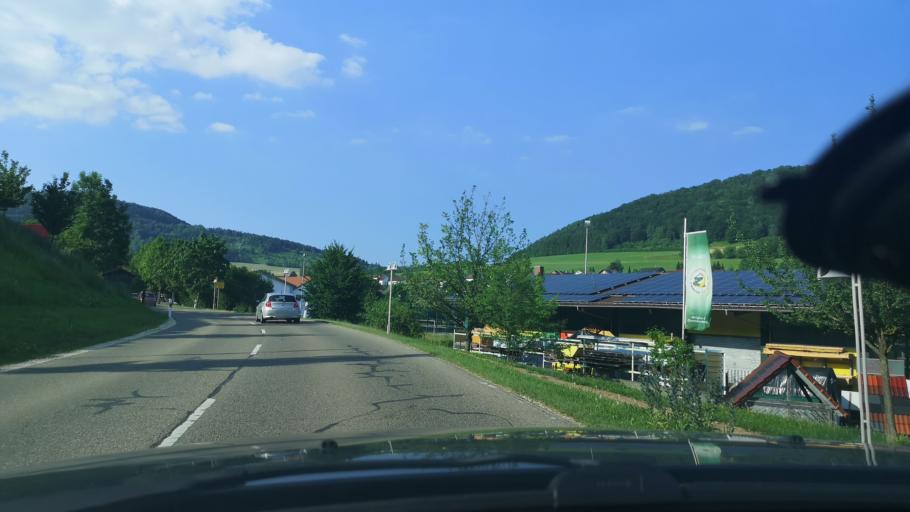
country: DE
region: Baden-Wuerttemberg
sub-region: Regierungsbezirk Stuttgart
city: Deggingen
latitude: 48.6103
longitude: 9.7351
